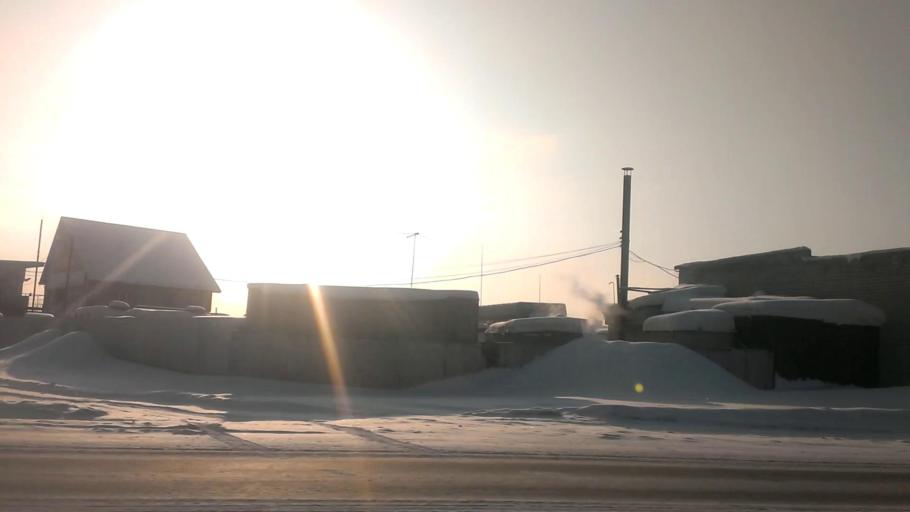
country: RU
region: Altai Krai
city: Novosilikatnyy
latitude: 53.3305
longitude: 83.6604
